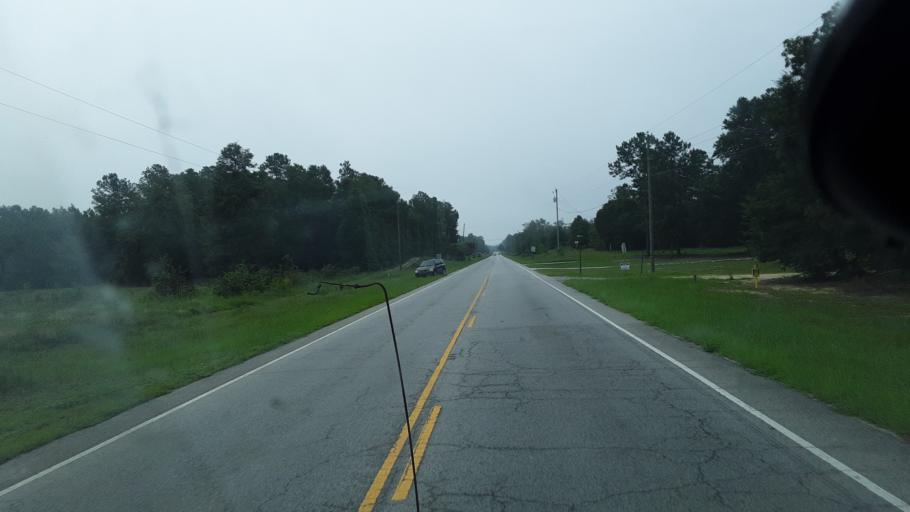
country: US
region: South Carolina
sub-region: Florence County
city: Johnsonville
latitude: 33.9106
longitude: -79.4056
